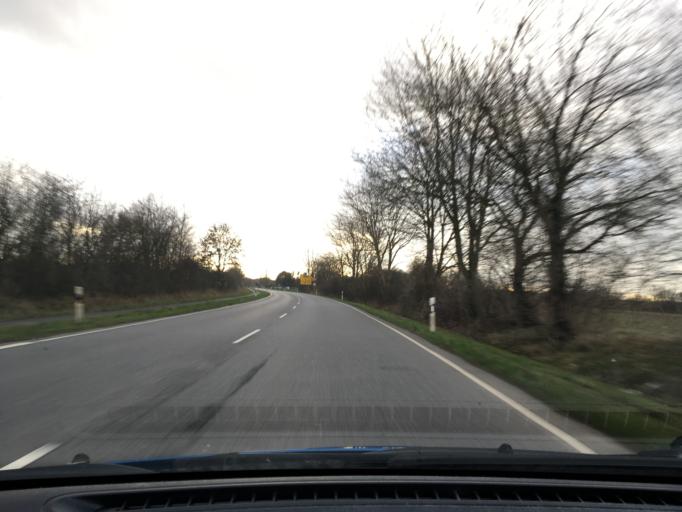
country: DE
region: Schleswig-Holstein
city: Ottenbuttel
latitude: 53.9763
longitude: 9.4972
